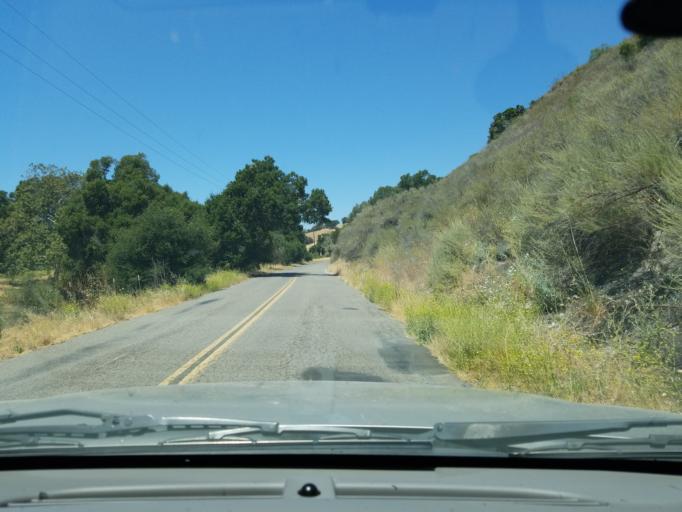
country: US
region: California
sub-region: Monterey County
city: Carmel Valley Village
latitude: 36.4375
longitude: -121.6326
